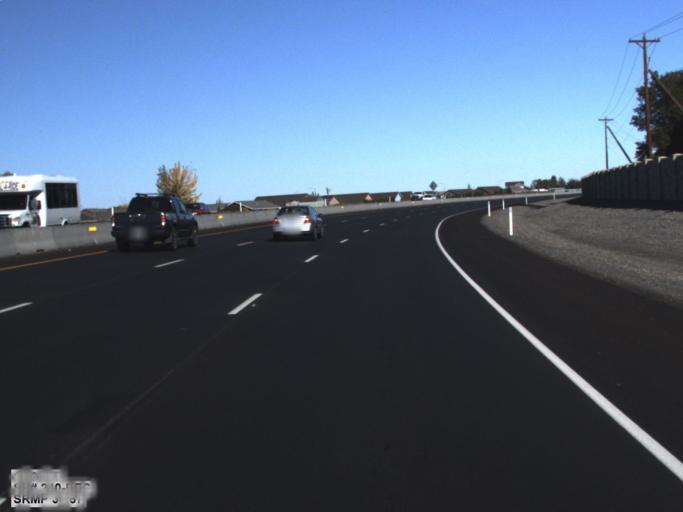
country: US
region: Washington
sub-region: Benton County
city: Richland
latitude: 46.2711
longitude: -119.3059
